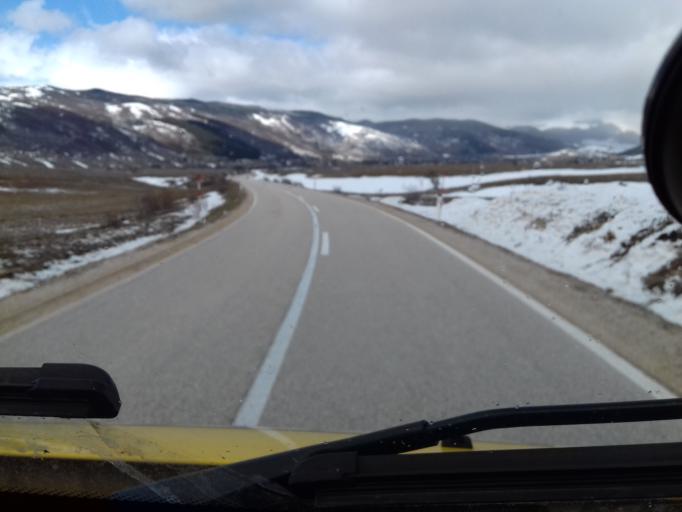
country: BA
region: Federation of Bosnia and Herzegovina
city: Tomislavgrad
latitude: 43.8124
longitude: 17.2032
